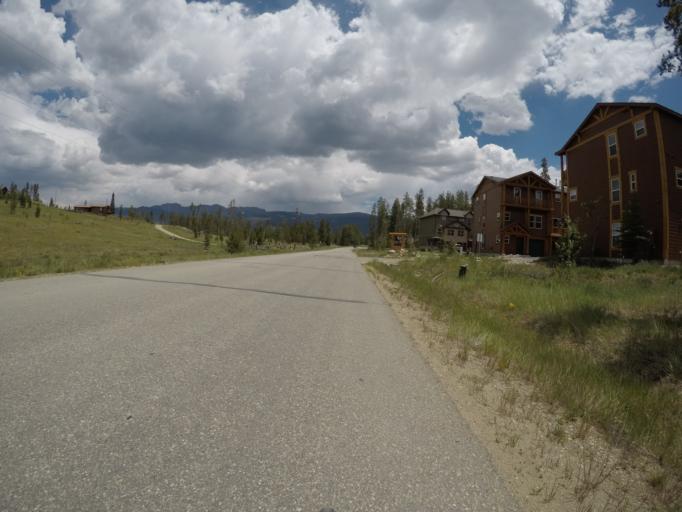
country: US
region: Colorado
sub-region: Grand County
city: Fraser
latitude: 39.9520
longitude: -105.7927
